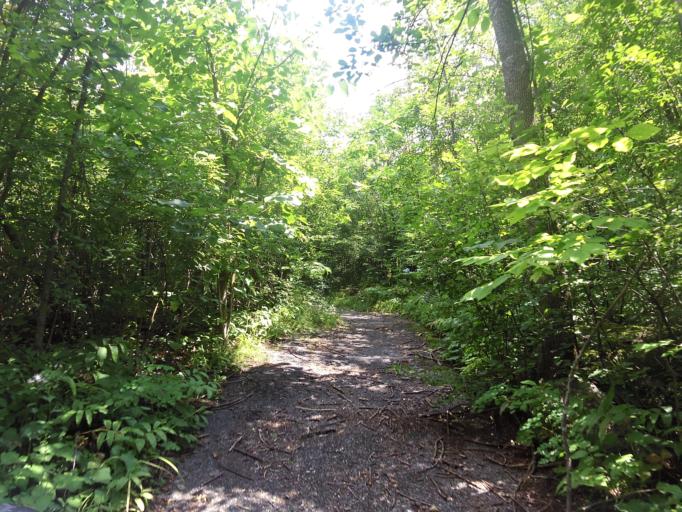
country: CA
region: Ontario
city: Bells Corners
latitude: 45.3182
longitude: -75.9211
